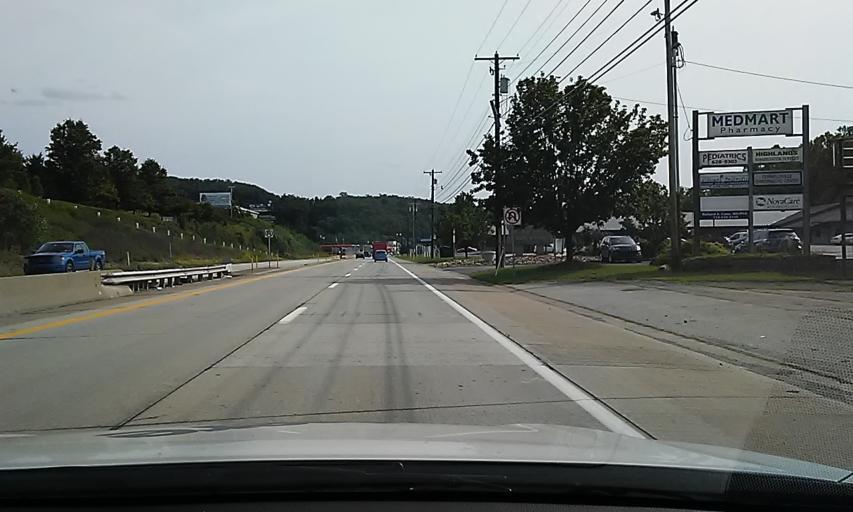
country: US
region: Pennsylvania
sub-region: Westmoreland County
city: Scottdale
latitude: 40.0598
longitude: -79.5627
